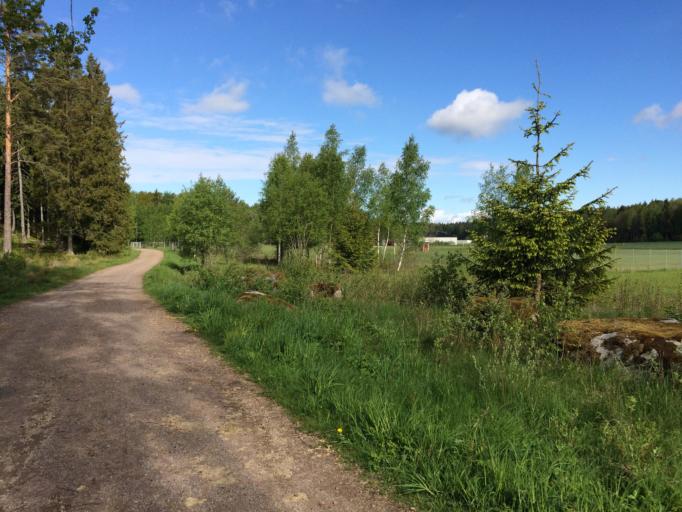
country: SE
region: Vaestmanland
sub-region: Hallstahammars Kommun
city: Hallstahammar
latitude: 59.6185
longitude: 16.2639
